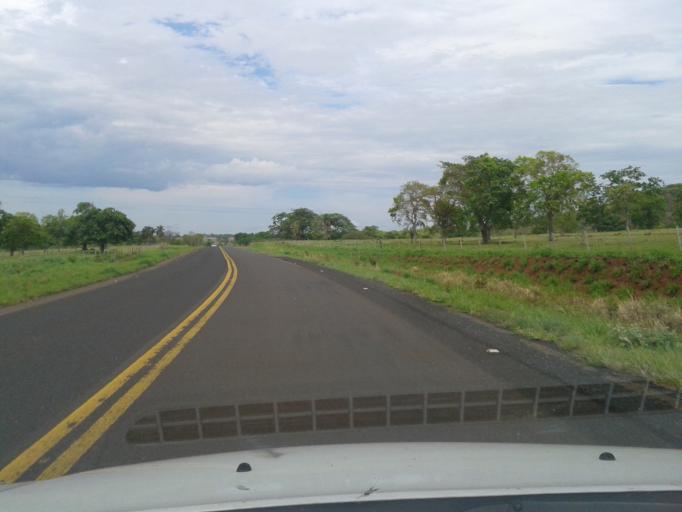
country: BR
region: Minas Gerais
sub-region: Iturama
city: Iturama
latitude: -19.5763
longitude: -49.9307
